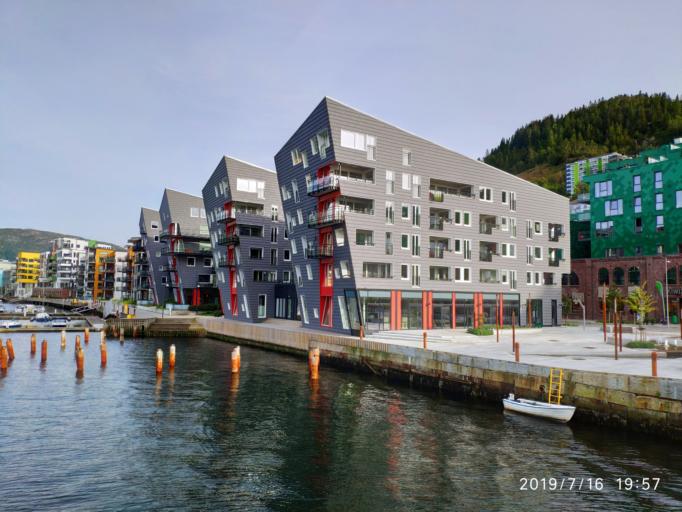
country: NO
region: Hordaland
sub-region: Bergen
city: Bergen
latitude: 60.3803
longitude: 5.3251
